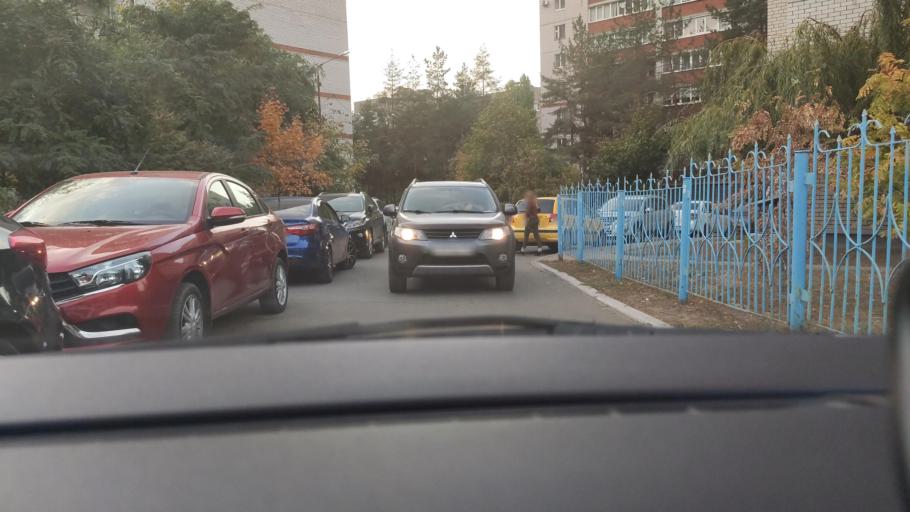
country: RU
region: Voronezj
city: Podgornoye
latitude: 51.7099
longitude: 39.1486
